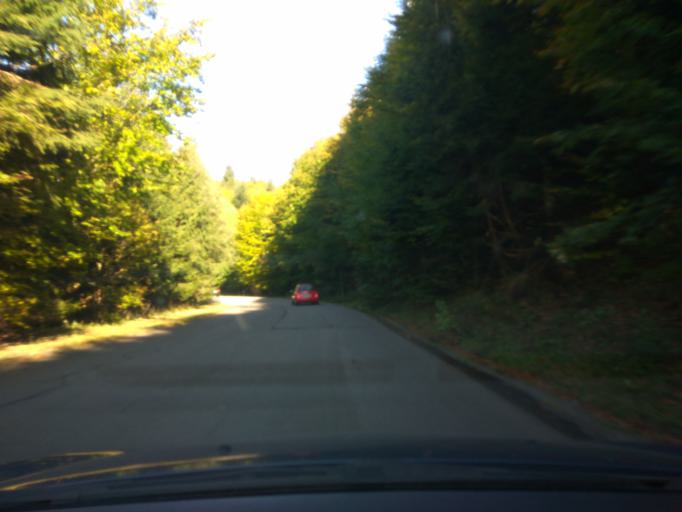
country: SK
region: Banskobystricky
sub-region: Okres Ziar nad Hronom
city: Kremnica
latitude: 48.7330
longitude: 18.9945
